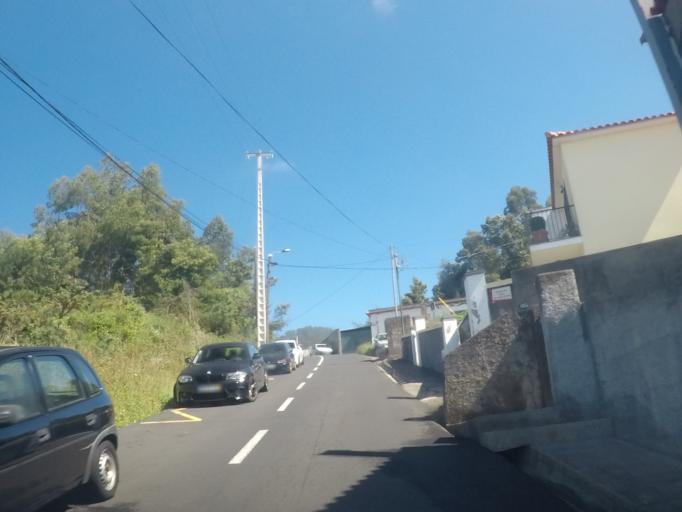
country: PT
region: Madeira
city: Camara de Lobos
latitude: 32.6768
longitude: -16.9655
